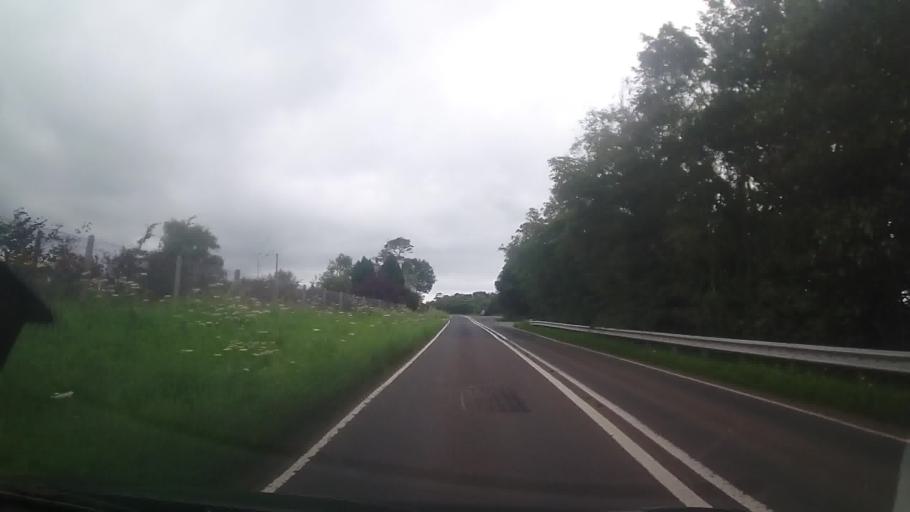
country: GB
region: Wales
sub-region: Gwynedd
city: Y Felinheli
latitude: 53.1933
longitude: -4.2433
